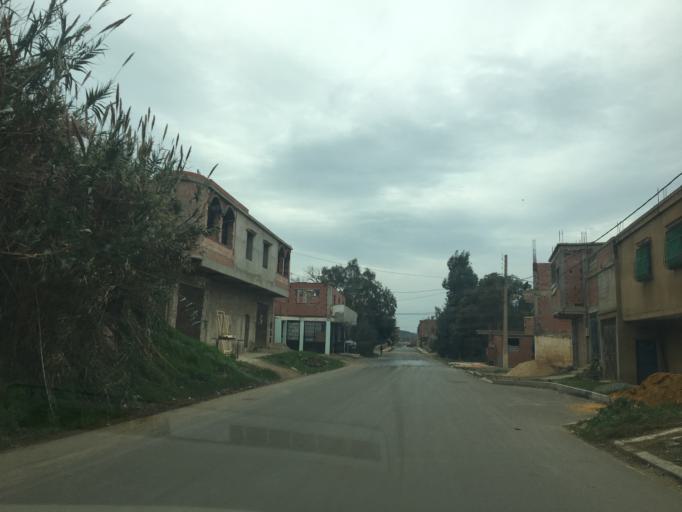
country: DZ
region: Tipaza
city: Tipasa
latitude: 36.6275
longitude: 2.2793
